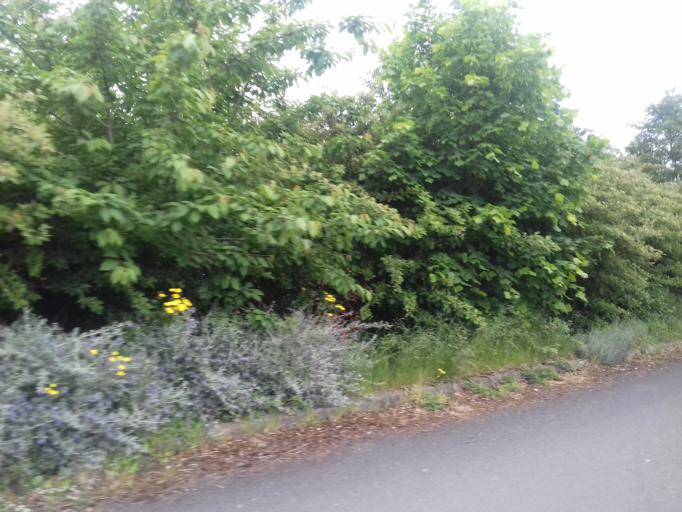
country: IE
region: Leinster
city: Donabate
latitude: 53.4930
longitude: -6.1748
